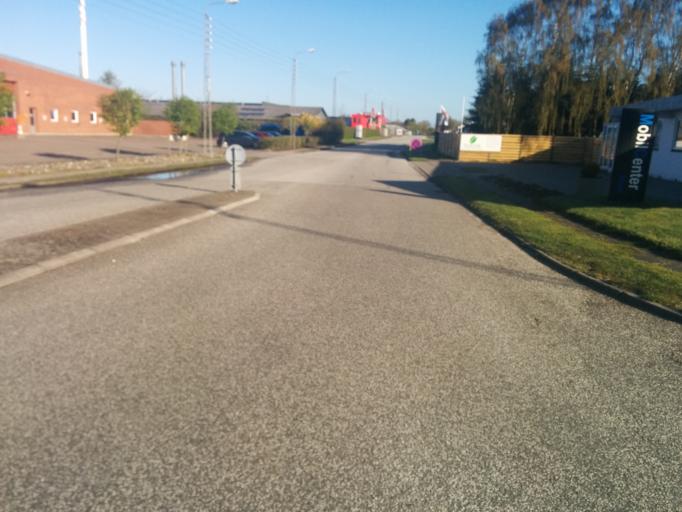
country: DK
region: Central Jutland
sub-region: Viborg Kommune
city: Viborg
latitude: 56.4680
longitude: 9.4020
